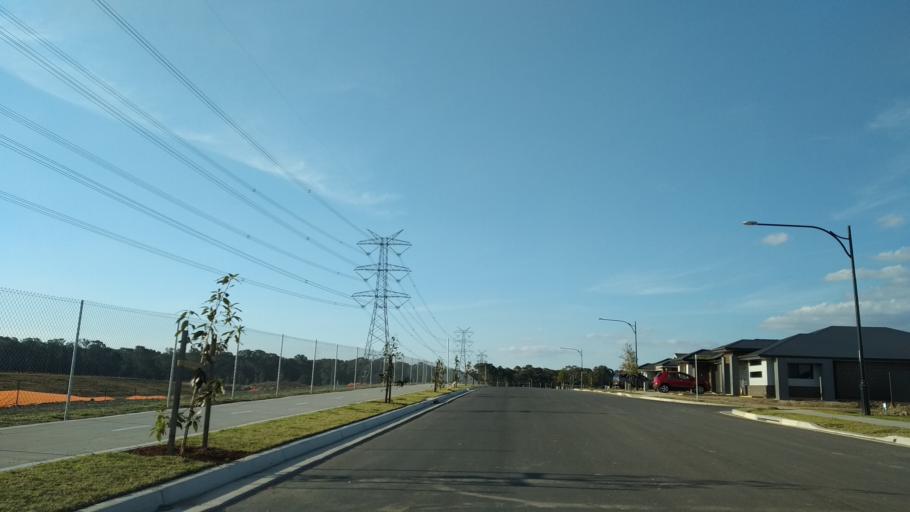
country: AU
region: New South Wales
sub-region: Penrith Municipality
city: Werrington County
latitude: -33.7294
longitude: 150.7549
